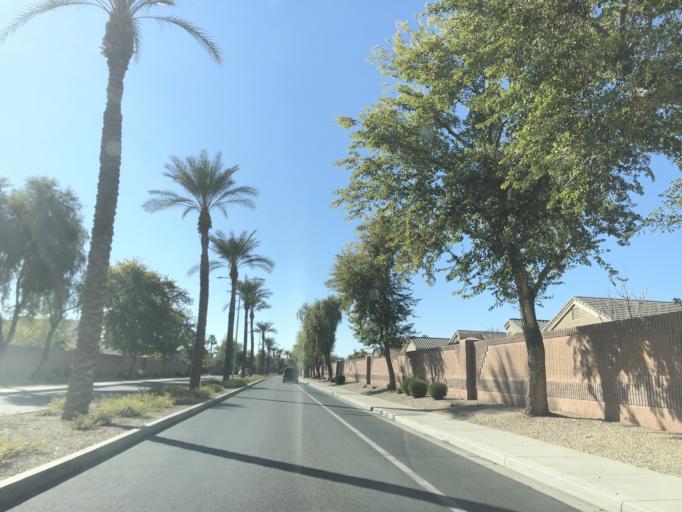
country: US
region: Arizona
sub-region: Maricopa County
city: El Mirage
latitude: 33.6184
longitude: -112.3294
